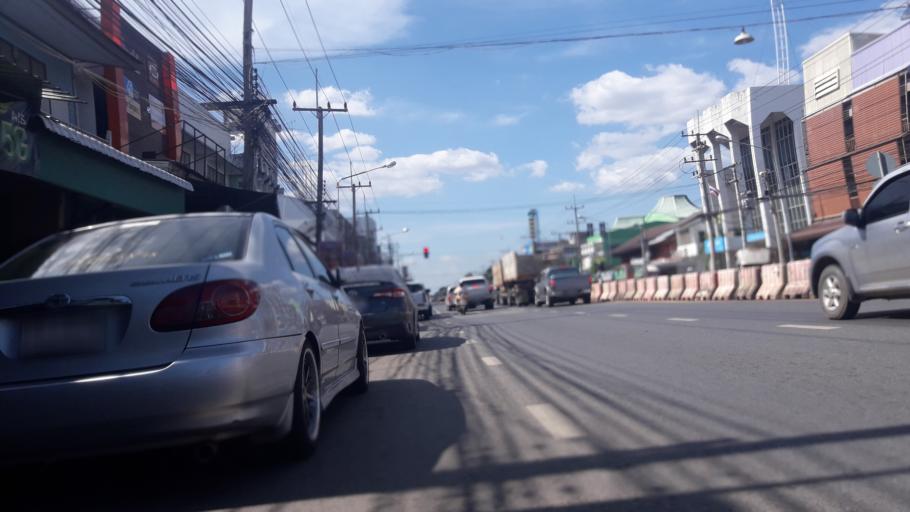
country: TH
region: Phichit
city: Thap Khlo
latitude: 16.1684
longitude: 100.5768
